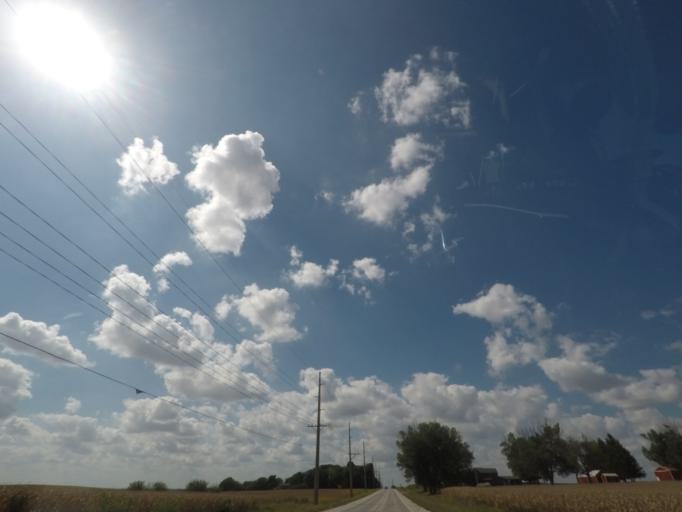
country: US
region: Iowa
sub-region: Story County
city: Ames
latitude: 42.0231
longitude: -93.5448
